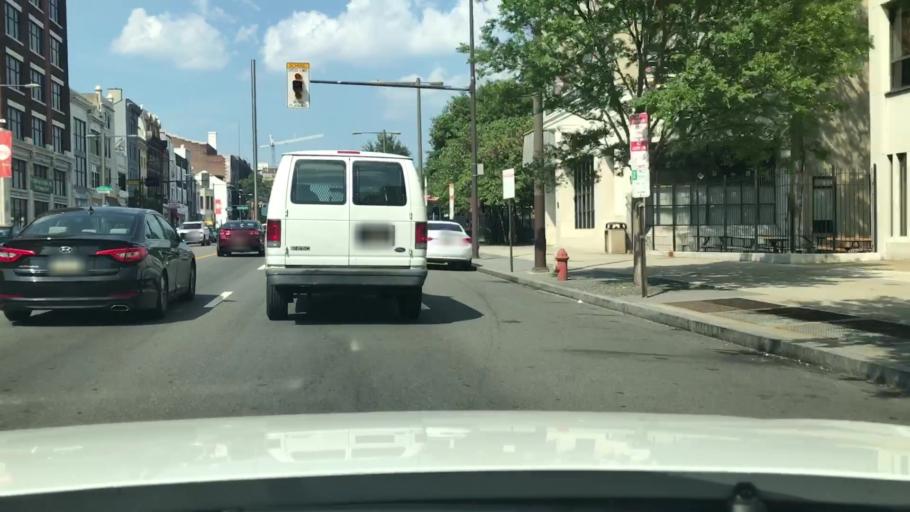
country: US
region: Pennsylvania
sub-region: Philadelphia County
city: Philadelphia
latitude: 39.9672
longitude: -75.1603
